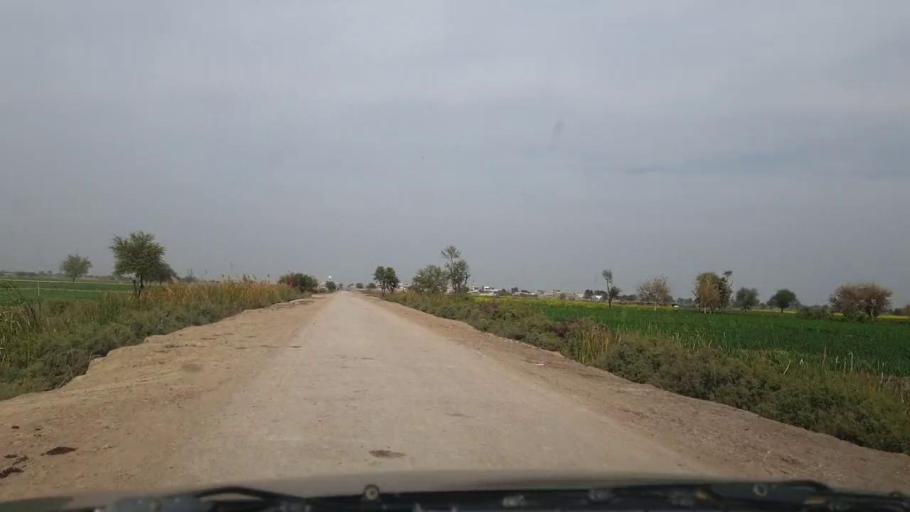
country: PK
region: Sindh
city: Sinjhoro
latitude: 26.0980
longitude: 68.8275
